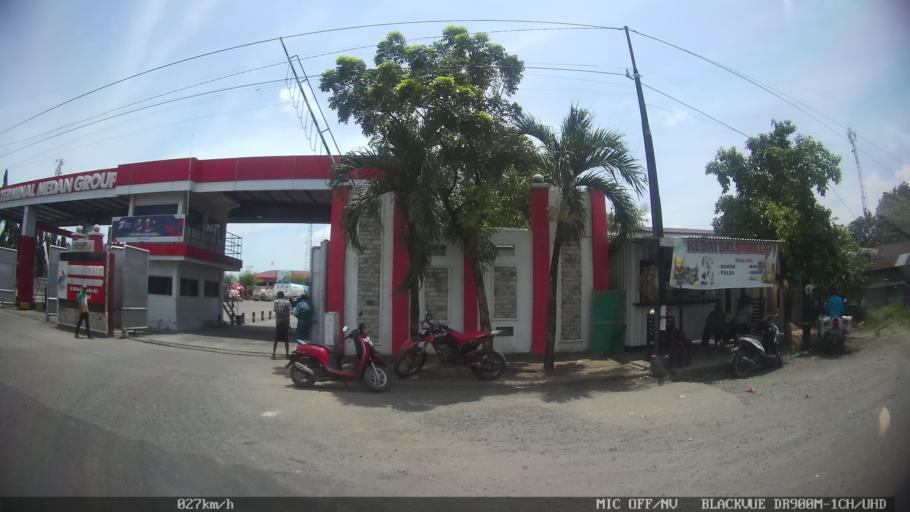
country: ID
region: North Sumatra
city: Labuhan Deli
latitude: 3.7480
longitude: 98.6748
